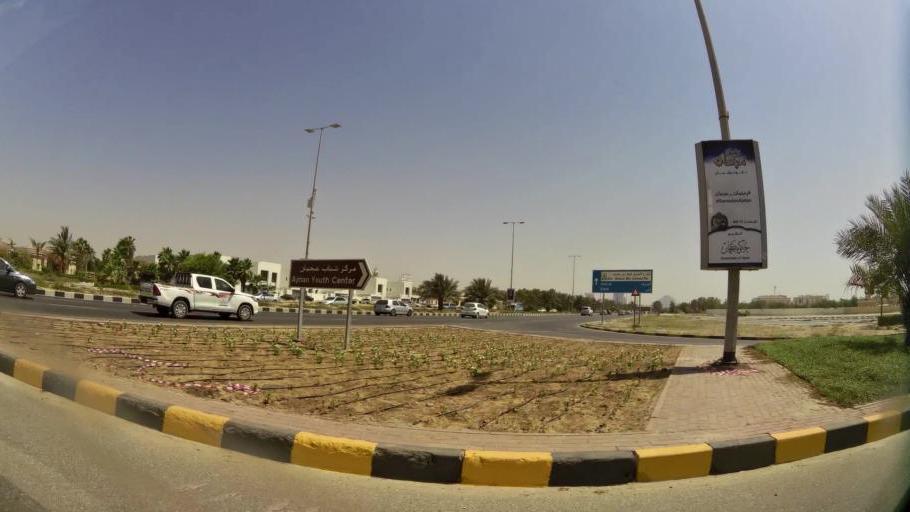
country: AE
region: Ajman
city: Ajman
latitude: 25.4155
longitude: 55.4860
